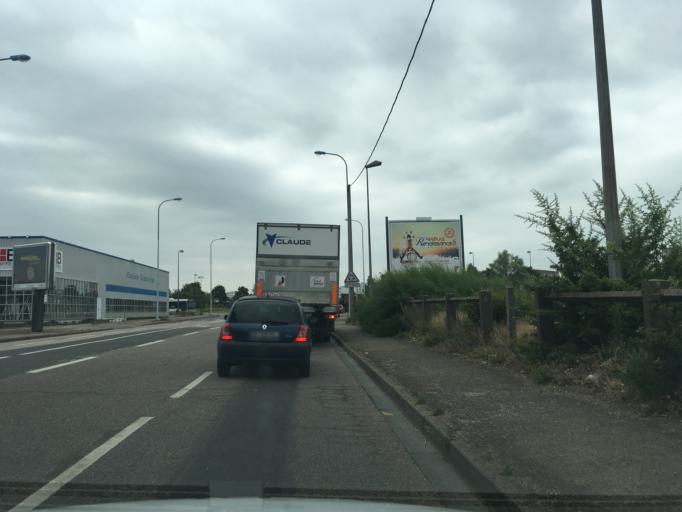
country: FR
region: Lorraine
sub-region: Departement de Meurthe-et-Moselle
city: Jarville-la-Malgrange
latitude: 48.6783
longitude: 6.2052
